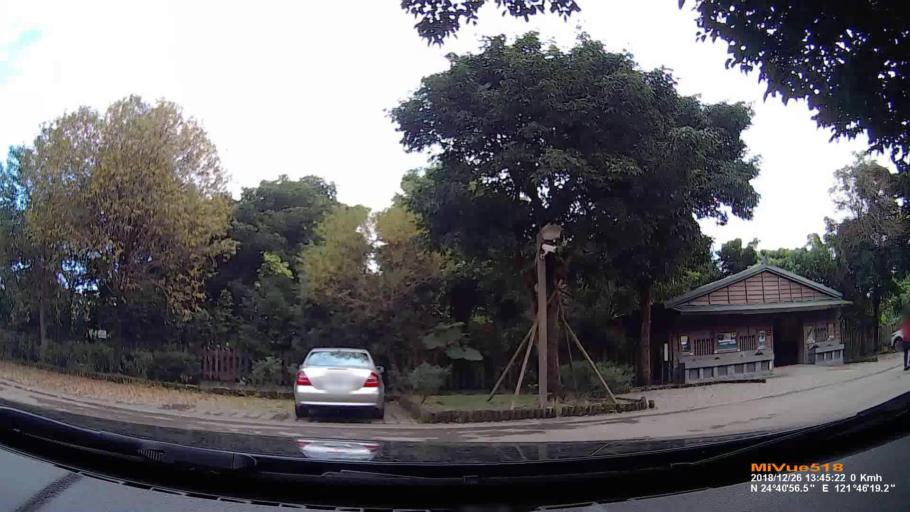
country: TW
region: Taiwan
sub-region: Yilan
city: Yilan
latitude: 24.6824
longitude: 121.7720
